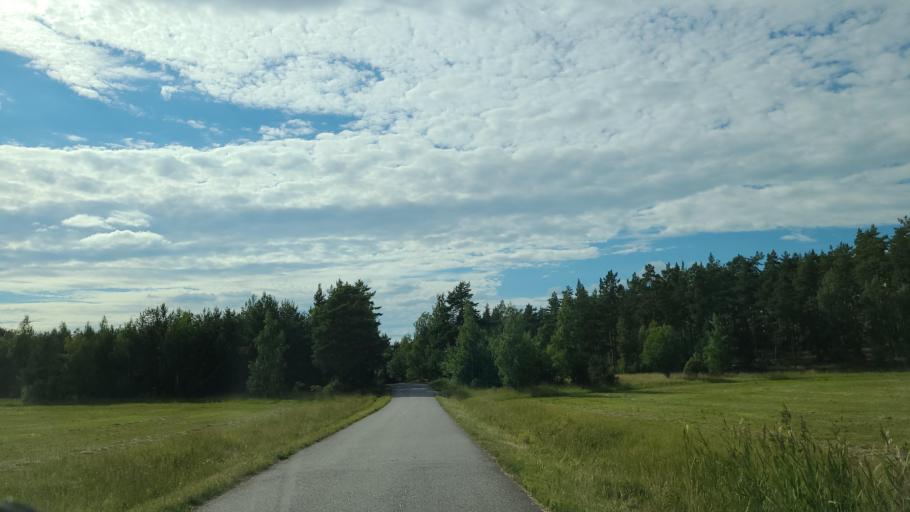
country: FI
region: Varsinais-Suomi
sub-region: Turku
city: Rymaettylae
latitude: 60.2905
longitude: 21.9502
